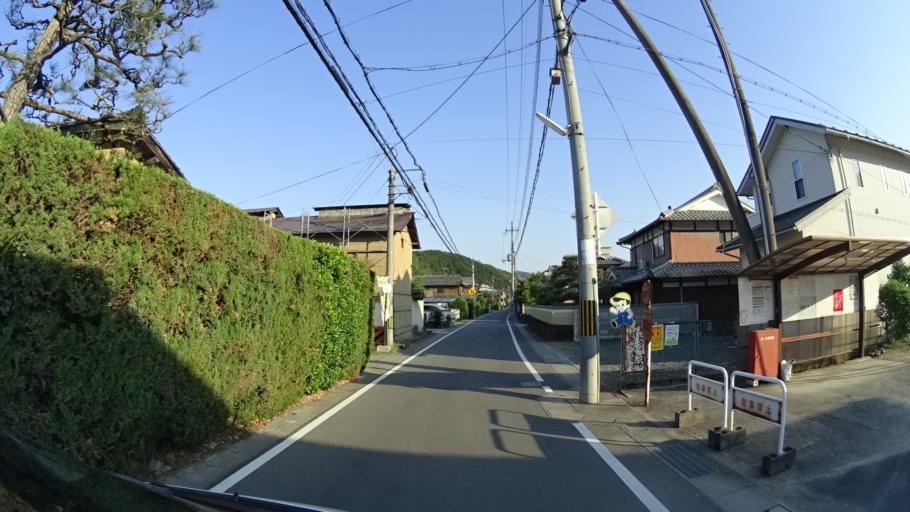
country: JP
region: Kyoto
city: Kameoka
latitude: 35.0904
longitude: 135.5103
